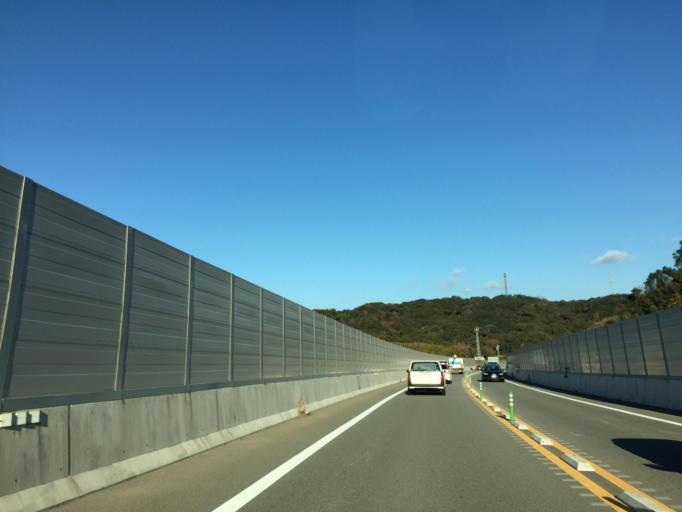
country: JP
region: Wakayama
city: Wakayama-shi
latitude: 34.2888
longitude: 135.1523
